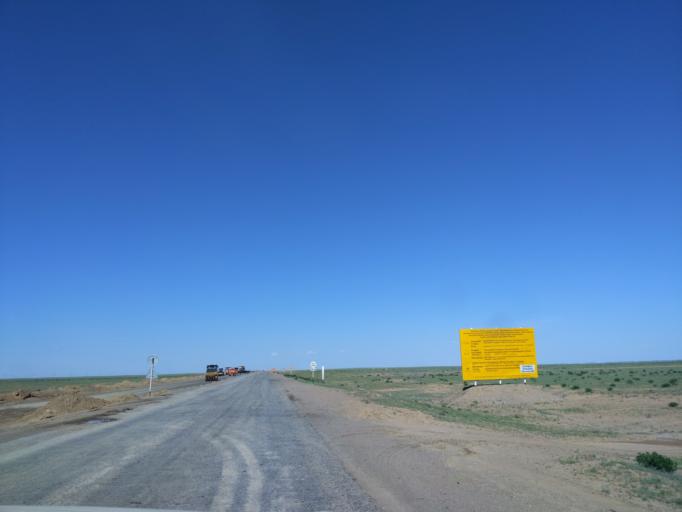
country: KZ
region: Almaty Oblysy
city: Bakanas
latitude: 44.3246
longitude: 75.4980
